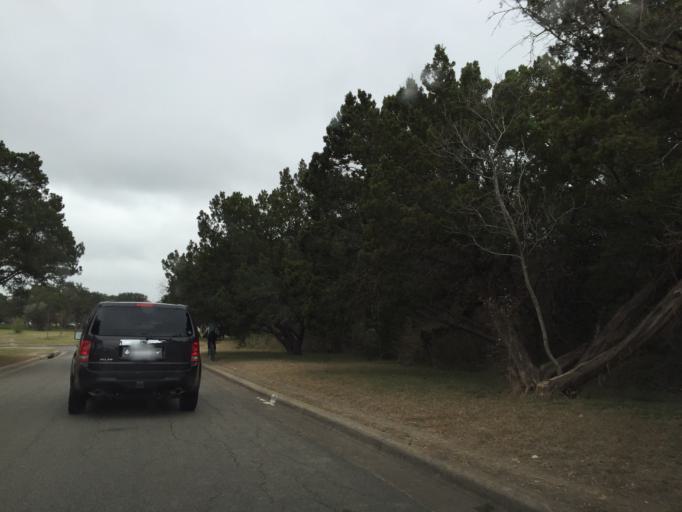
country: US
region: Texas
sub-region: Travis County
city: Wells Branch
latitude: 30.4030
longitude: -97.6861
